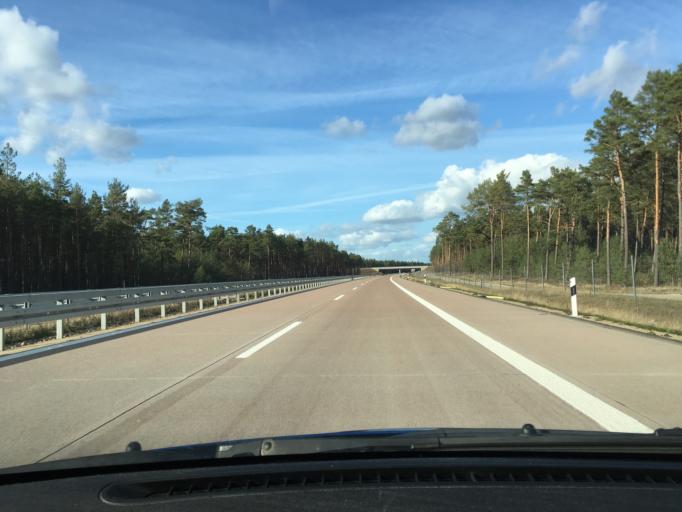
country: DE
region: Mecklenburg-Vorpommern
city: Grabow
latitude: 53.2724
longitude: 11.5287
